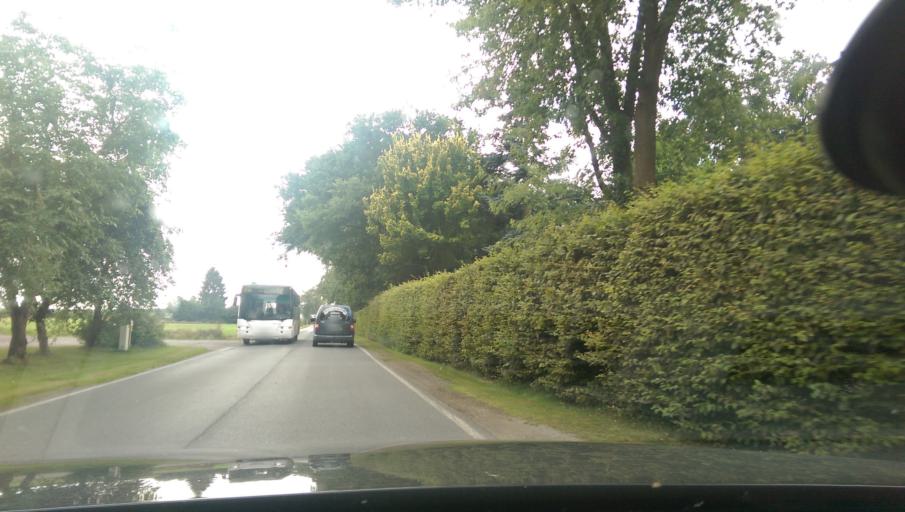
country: DE
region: Lower Saxony
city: Steimbke
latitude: 52.6173
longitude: 9.4846
